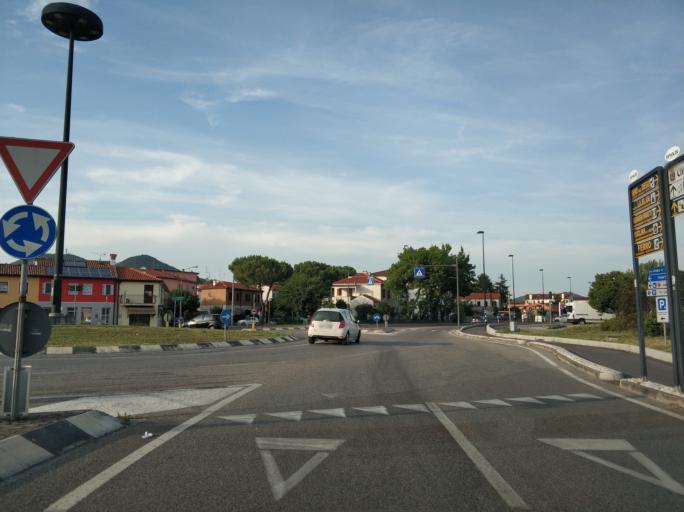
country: IT
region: Veneto
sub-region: Provincia di Padova
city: Este
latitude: 45.2223
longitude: 11.6593
